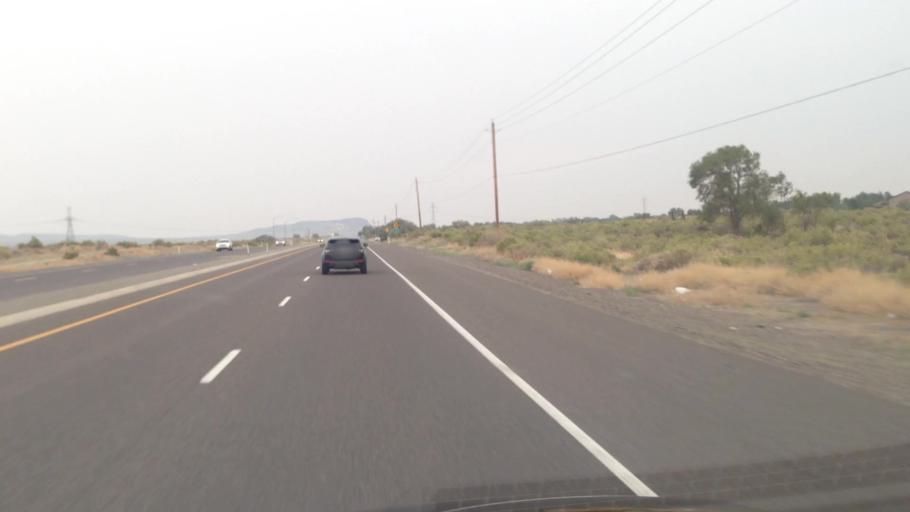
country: US
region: Nevada
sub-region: Lyon County
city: Fernley
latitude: 39.5950
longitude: -119.1729
